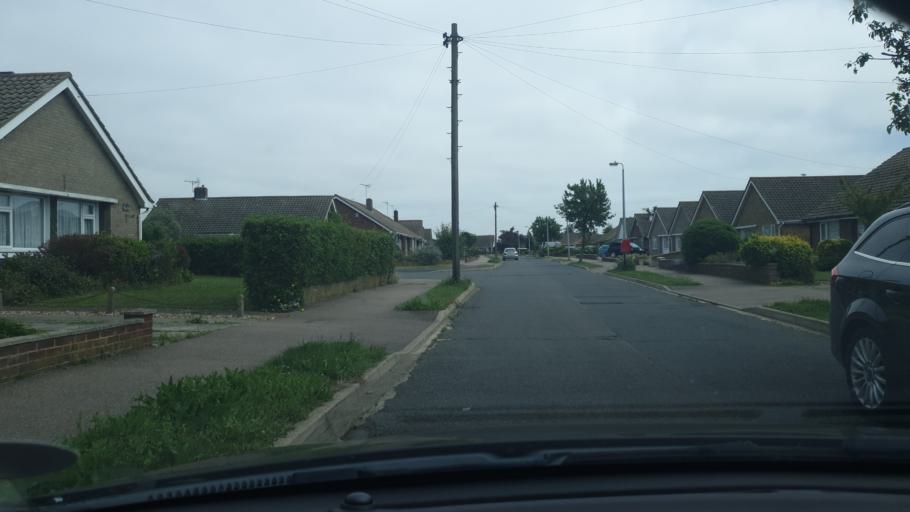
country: GB
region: England
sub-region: Essex
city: Frinton-on-Sea
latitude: 51.8402
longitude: 1.2257
